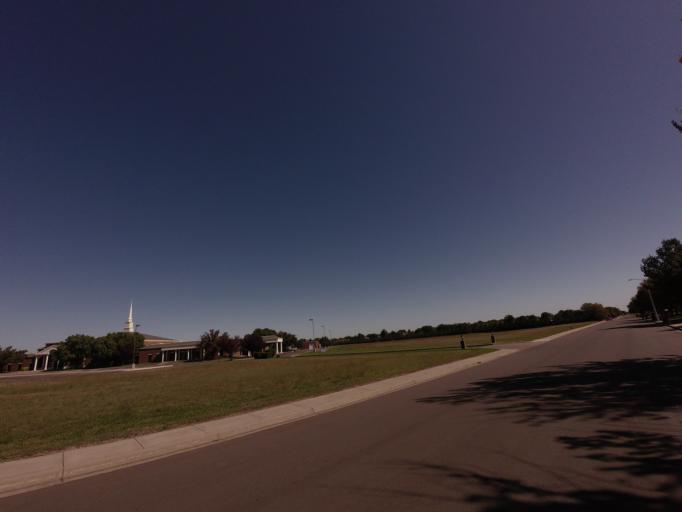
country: US
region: New Mexico
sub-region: Curry County
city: Clovis
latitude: 34.4232
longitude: -103.1772
